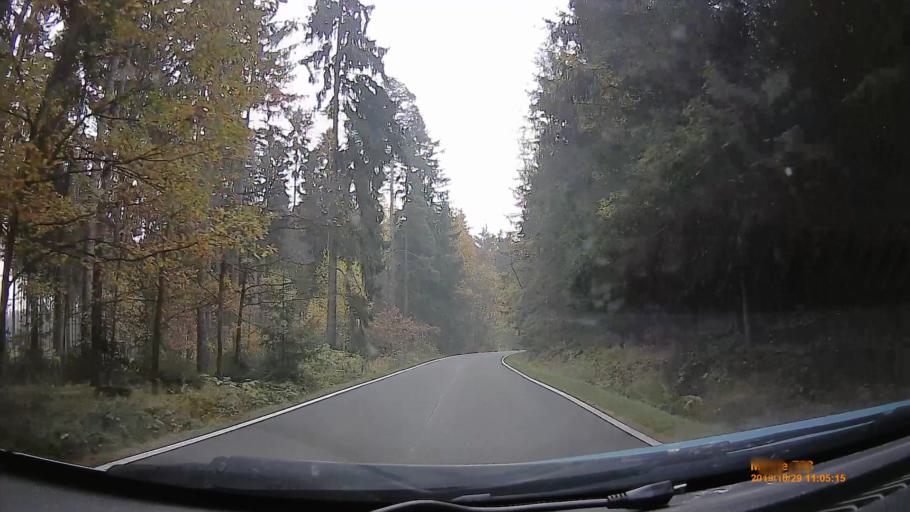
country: PL
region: Lower Silesian Voivodeship
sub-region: Powiat klodzki
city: Szczytna
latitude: 50.4724
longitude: 16.4744
